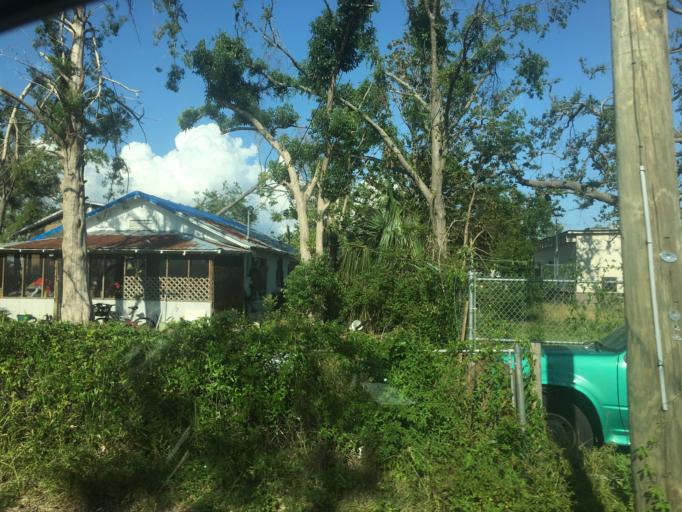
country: US
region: Florida
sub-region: Bay County
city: Cedar Grove
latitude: 30.1590
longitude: -85.6334
